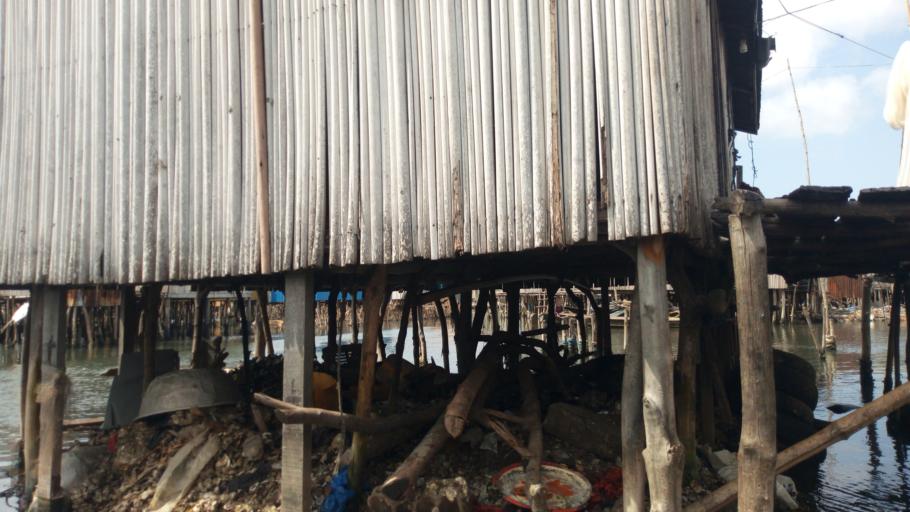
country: BJ
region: Littoral
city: Cotonou
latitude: 6.3912
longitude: 2.4331
